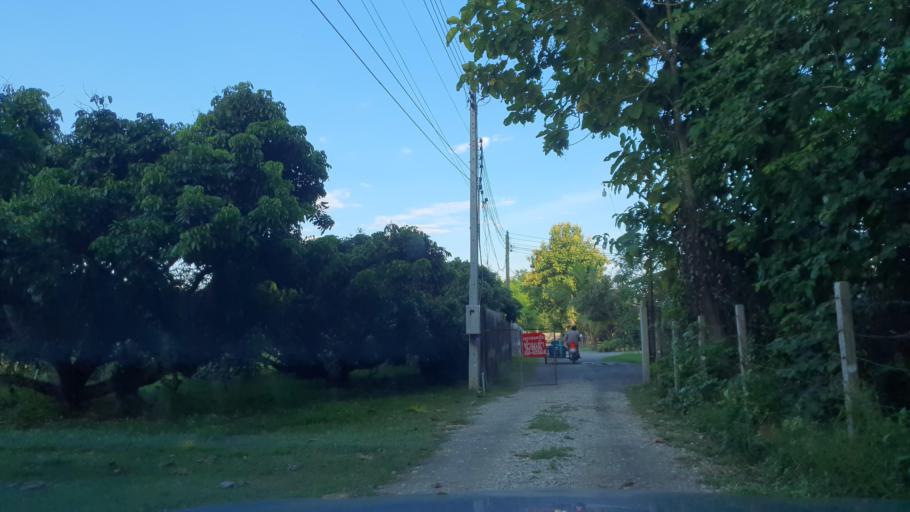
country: TH
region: Chiang Mai
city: Hang Dong
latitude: 18.6809
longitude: 98.8878
